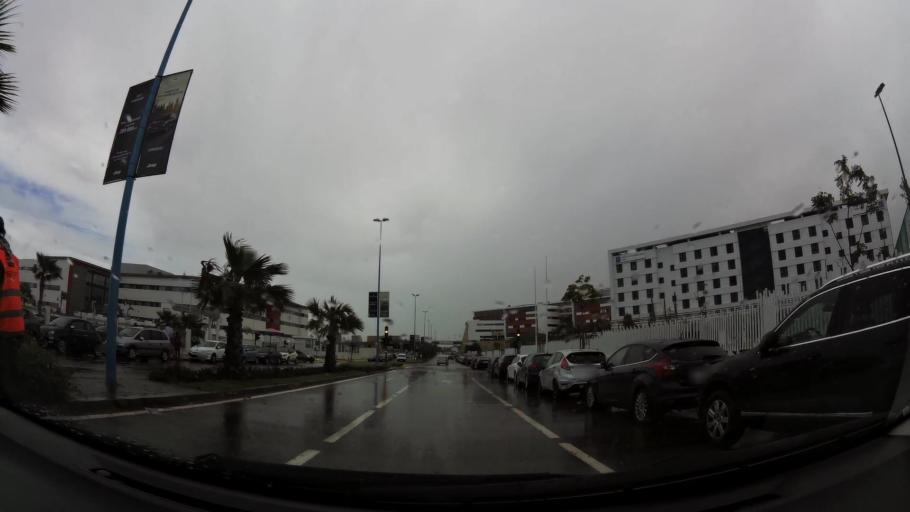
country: MA
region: Grand Casablanca
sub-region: Casablanca
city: Casablanca
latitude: 33.5510
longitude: -7.6690
